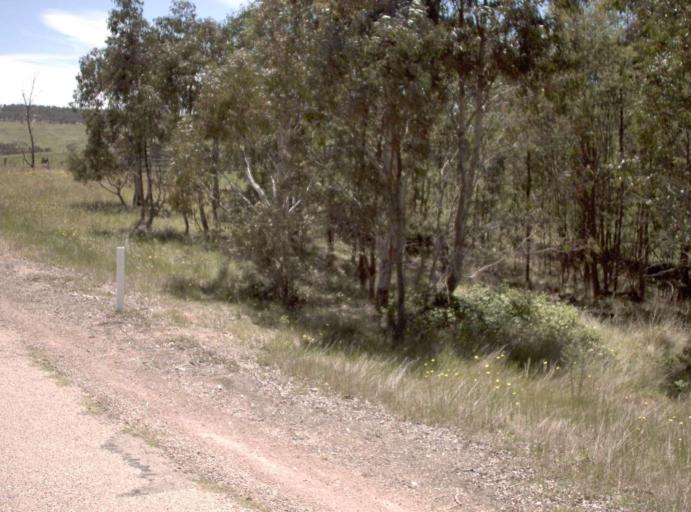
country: AU
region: New South Wales
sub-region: Snowy River
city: Jindabyne
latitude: -37.0549
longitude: 148.2593
